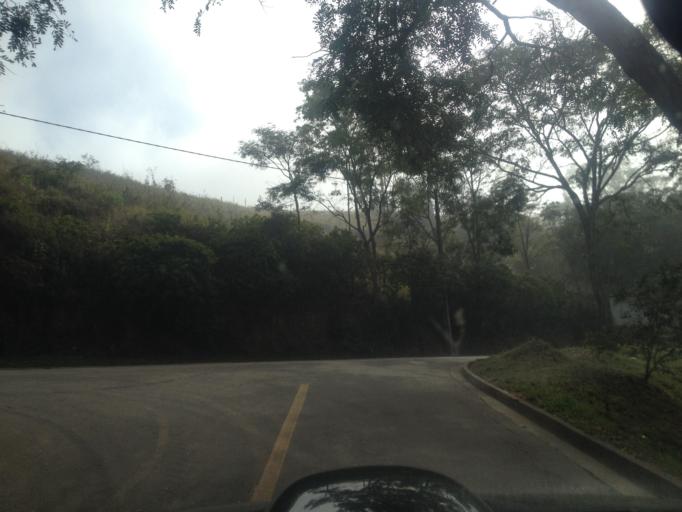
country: BR
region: Rio de Janeiro
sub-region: Porto Real
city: Porto Real
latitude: -22.4394
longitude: -44.3256
